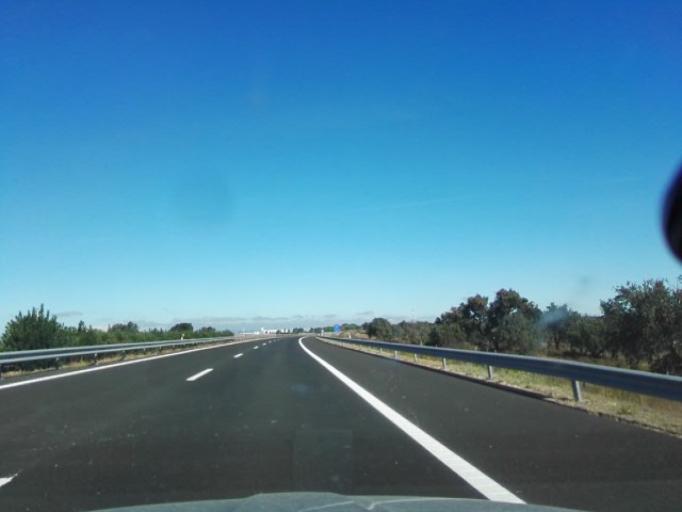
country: PT
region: Santarem
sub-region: Benavente
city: Benavente
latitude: 38.9296
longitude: -8.8164
